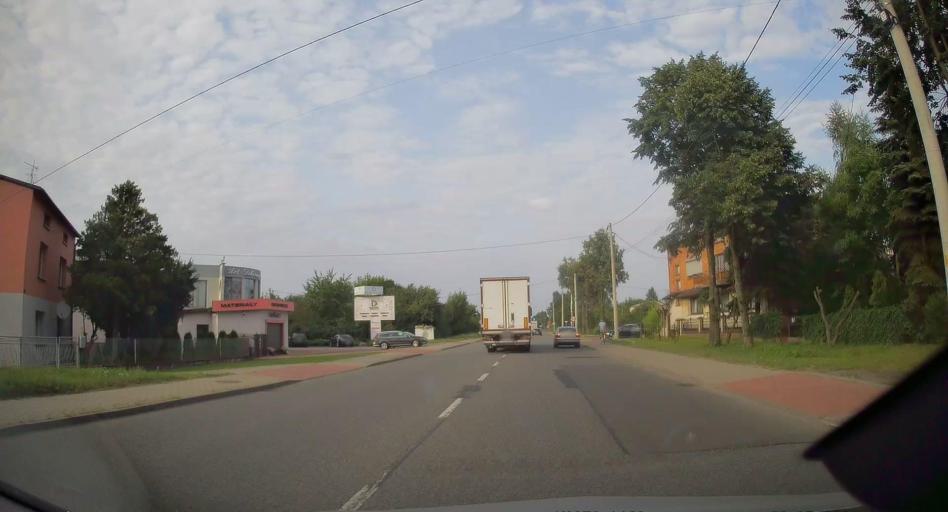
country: PL
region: Silesian Voivodeship
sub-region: Powiat czestochowski
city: Redziny
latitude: 50.8639
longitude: 19.2243
